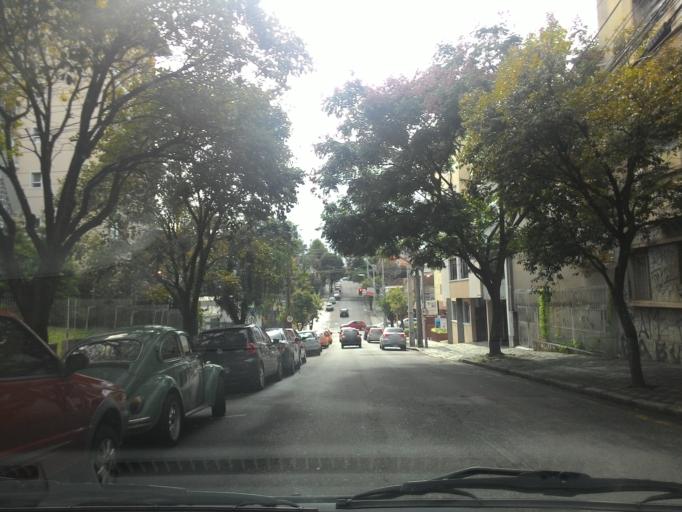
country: BR
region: Parana
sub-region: Curitiba
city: Curitiba
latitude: -25.4241
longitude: -49.2761
